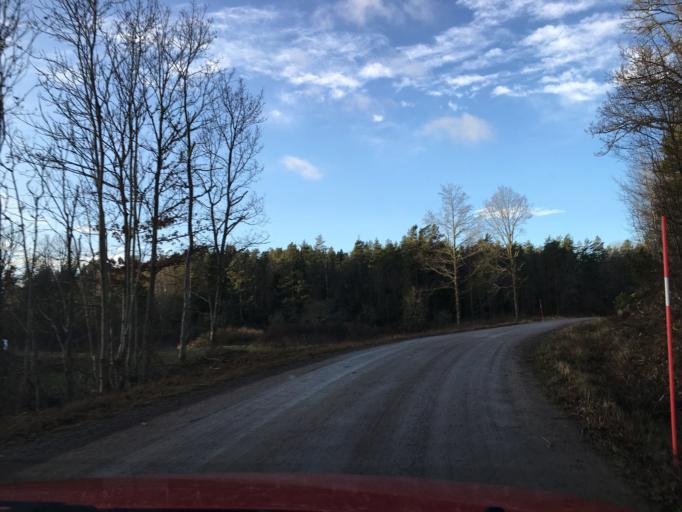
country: SE
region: Kalmar
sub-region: Vasterviks Kommun
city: Vaestervik
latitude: 57.6385
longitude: 16.4944
